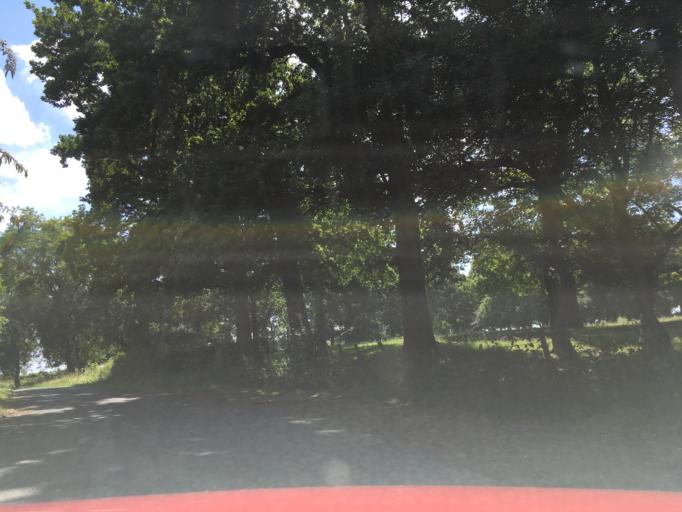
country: GB
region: Wales
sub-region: Newport
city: Llanwern
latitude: 51.5956
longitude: -2.9127
